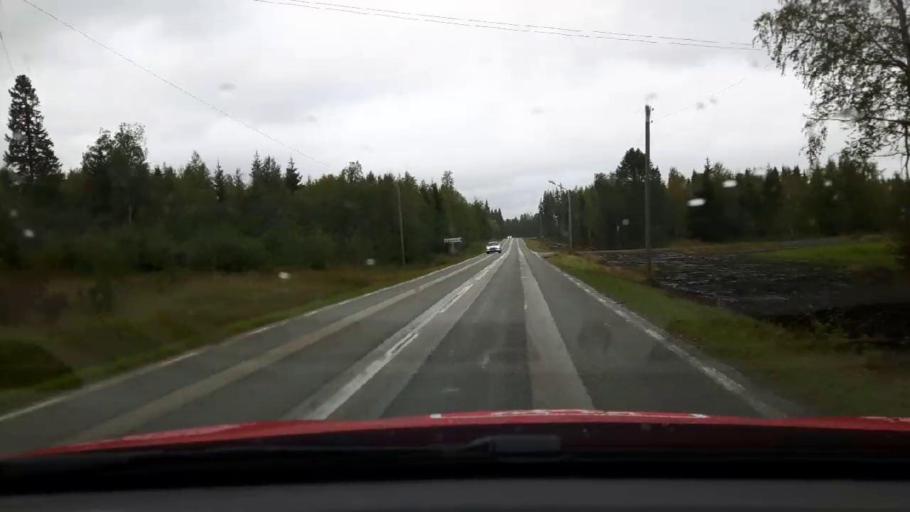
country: SE
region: Jaemtland
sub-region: Bergs Kommun
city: Hoverberg
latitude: 62.8185
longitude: 14.3987
